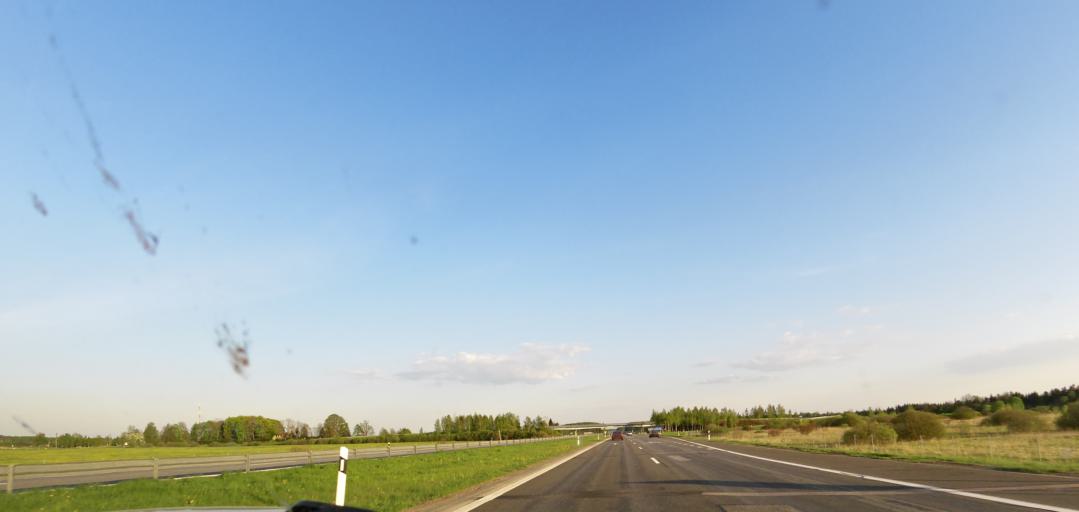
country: LT
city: Sirvintos
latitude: 55.0192
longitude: 24.9105
